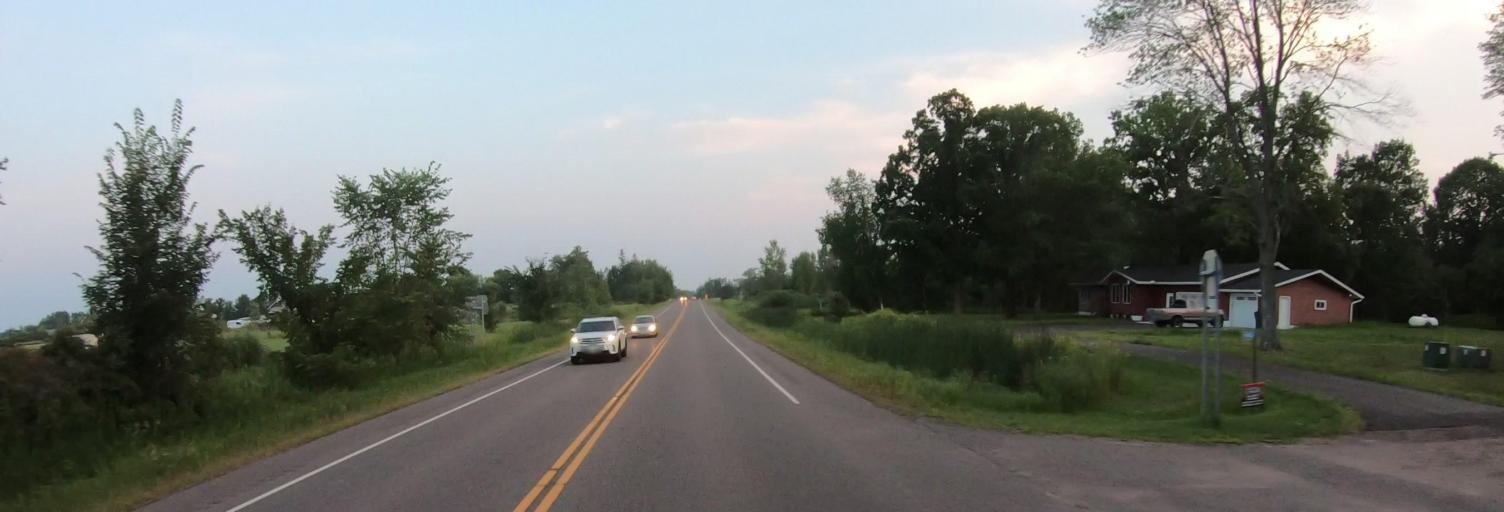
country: US
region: Minnesota
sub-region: Pine County
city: Rock Creek
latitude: 45.7714
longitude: -92.9602
